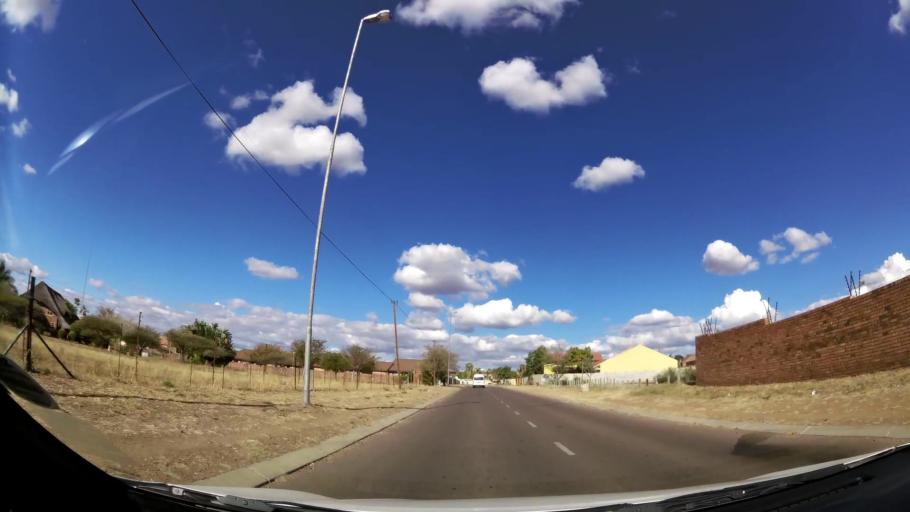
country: ZA
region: Limpopo
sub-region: Capricorn District Municipality
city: Polokwane
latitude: -23.8796
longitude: 29.4876
